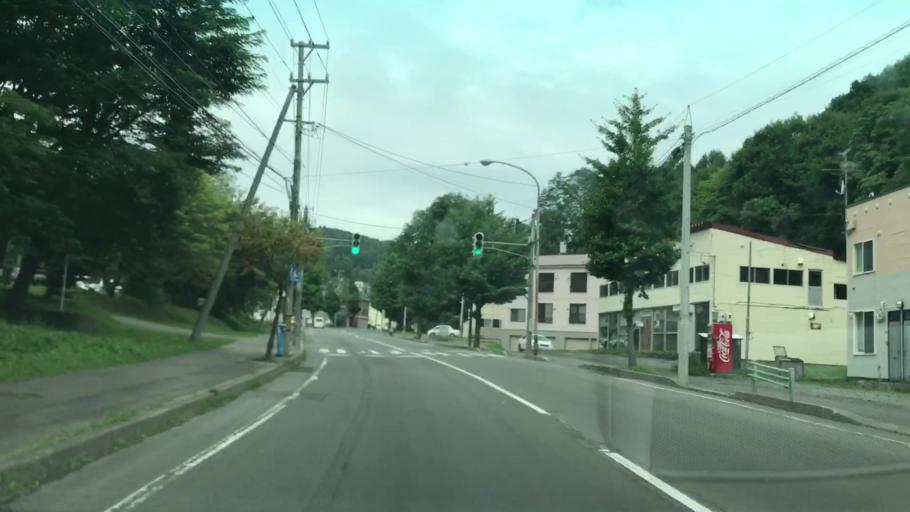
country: JP
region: Hokkaido
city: Otaru
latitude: 43.2117
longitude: 140.9657
